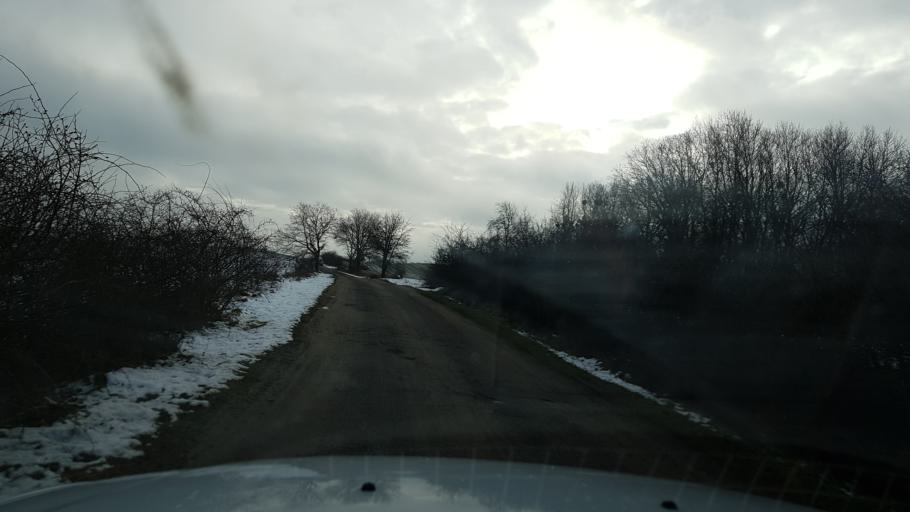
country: PL
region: West Pomeranian Voivodeship
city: Trzcinsko Zdroj
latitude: 52.9514
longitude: 14.6934
